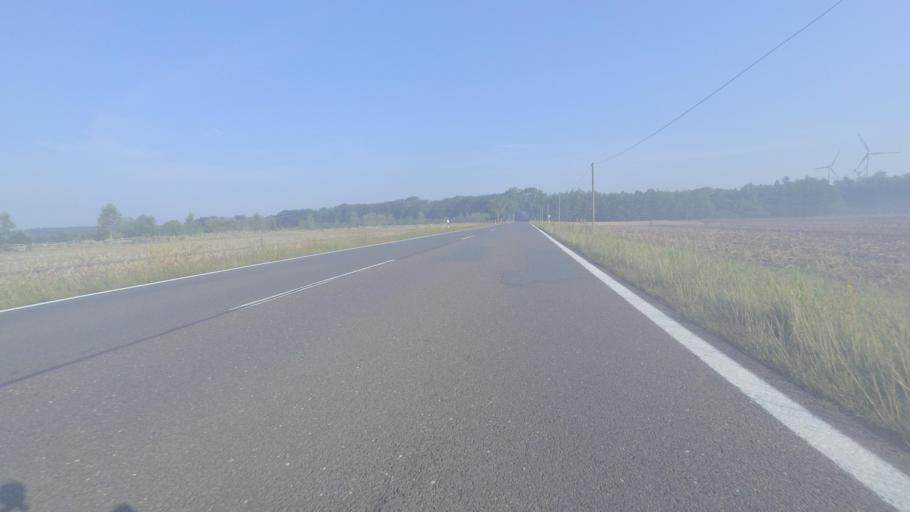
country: DE
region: Mecklenburg-Vorpommern
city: Grimmen
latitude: 54.0333
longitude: 13.1294
